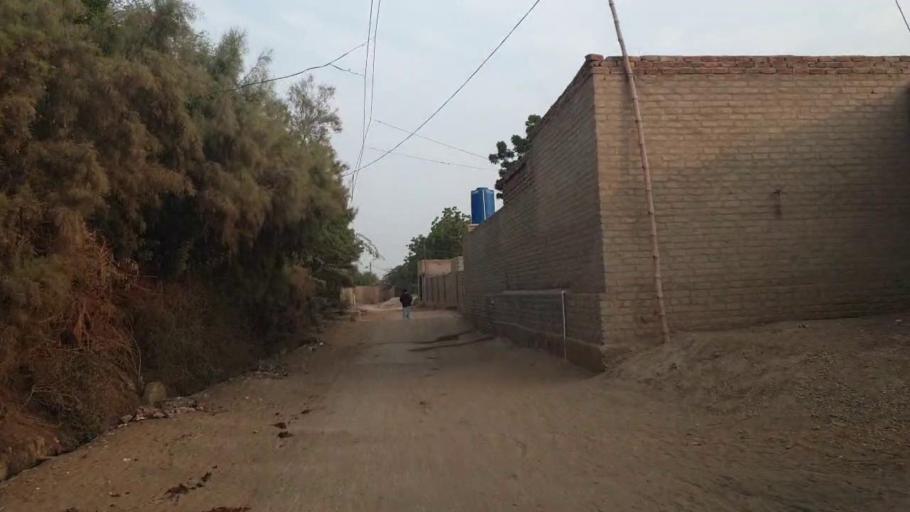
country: PK
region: Sindh
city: Sann
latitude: 26.1716
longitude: 68.0178
